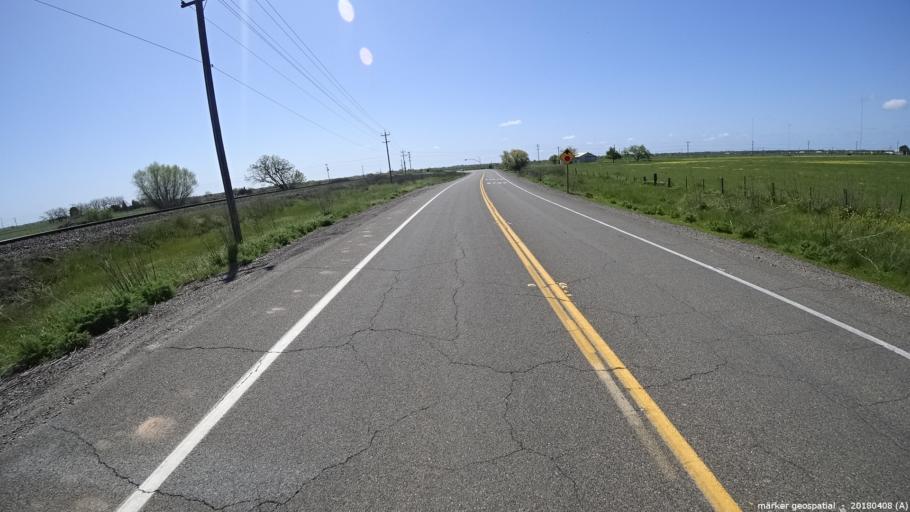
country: US
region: California
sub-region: San Joaquin County
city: Thornton
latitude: 38.2925
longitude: -121.4414
